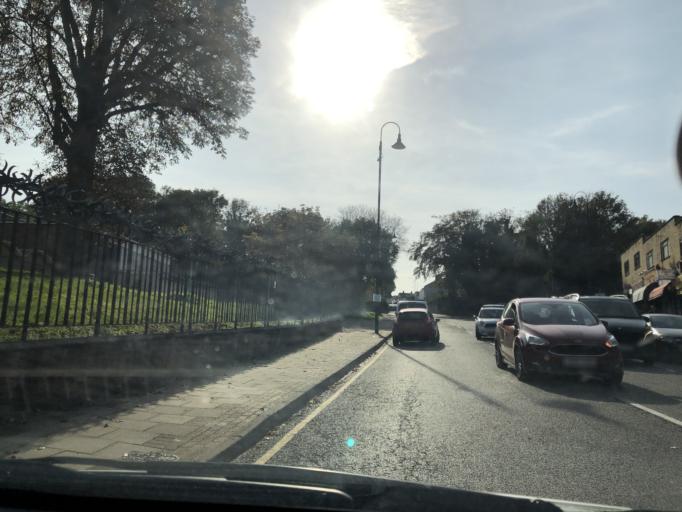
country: GB
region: England
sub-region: Greater London
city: Erith
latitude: 51.4498
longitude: 0.1819
